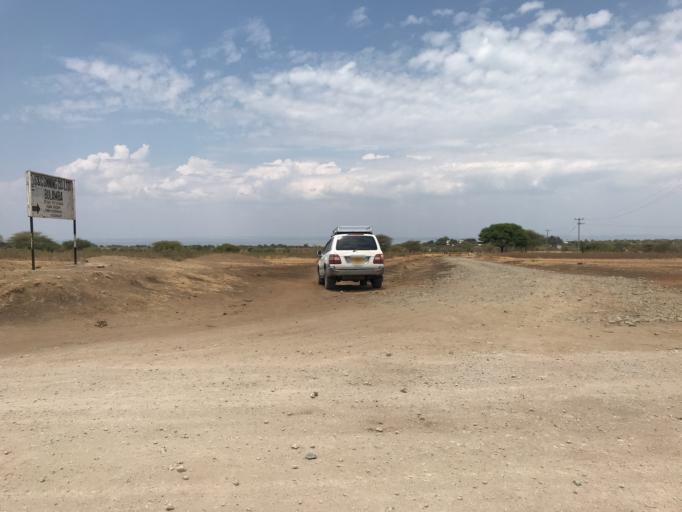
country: TZ
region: Mara
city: Kibara
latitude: -2.1291
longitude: 33.6355
